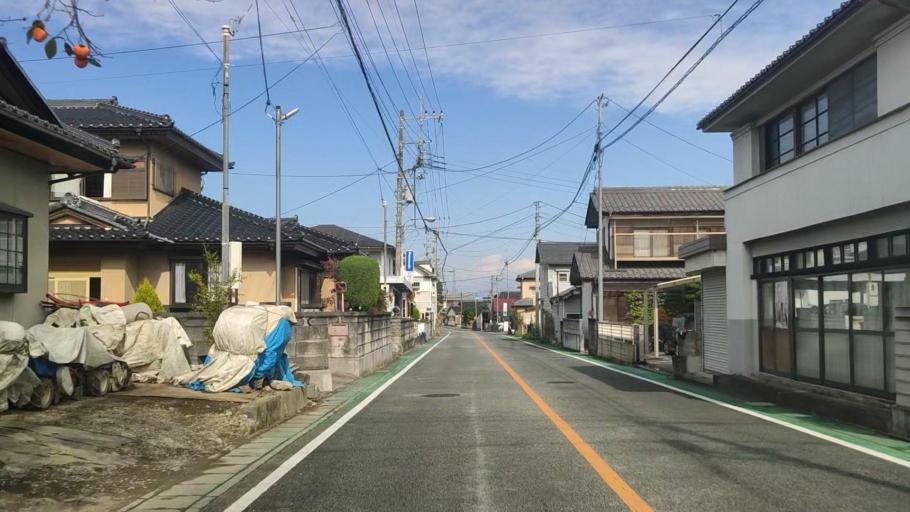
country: JP
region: Yamanashi
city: Ryuo
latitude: 35.5686
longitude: 138.4648
